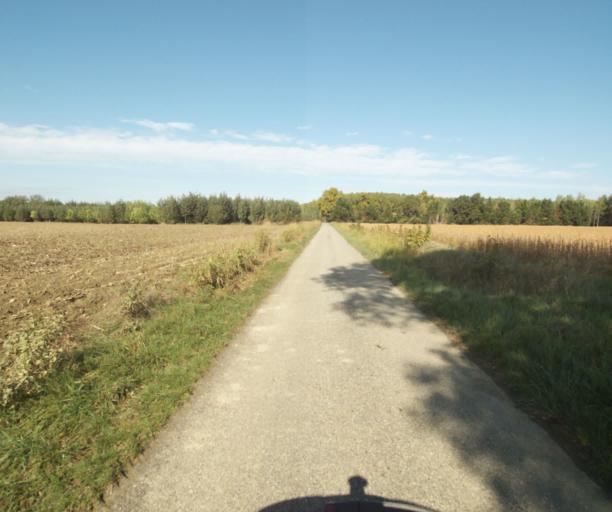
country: FR
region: Midi-Pyrenees
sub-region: Departement du Tarn-et-Garonne
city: Finhan
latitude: 43.8986
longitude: 1.2188
